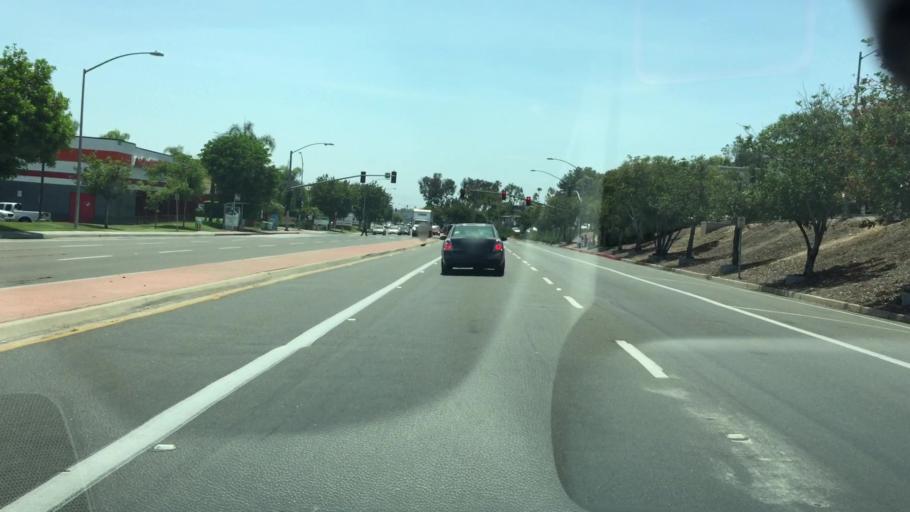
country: US
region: California
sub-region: San Diego County
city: Lemon Grove
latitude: 32.7509
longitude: -117.0696
